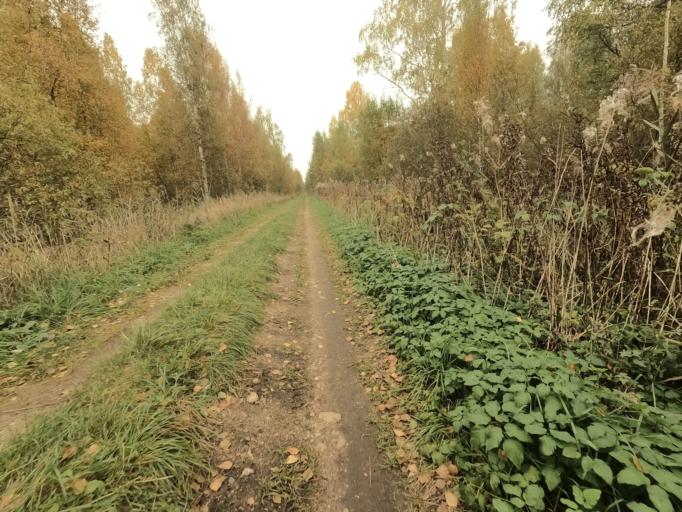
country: RU
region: Novgorod
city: Pankovka
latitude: 58.8898
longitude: 30.9491
